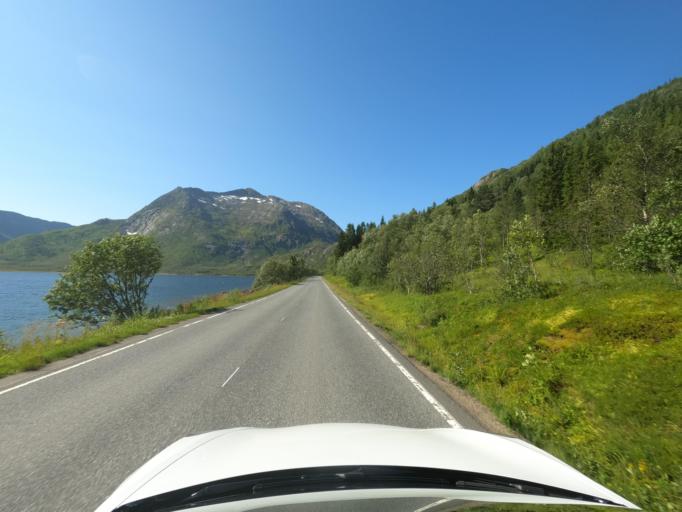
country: NO
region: Nordland
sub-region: Lodingen
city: Lodingen
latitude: 68.5456
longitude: 15.7403
